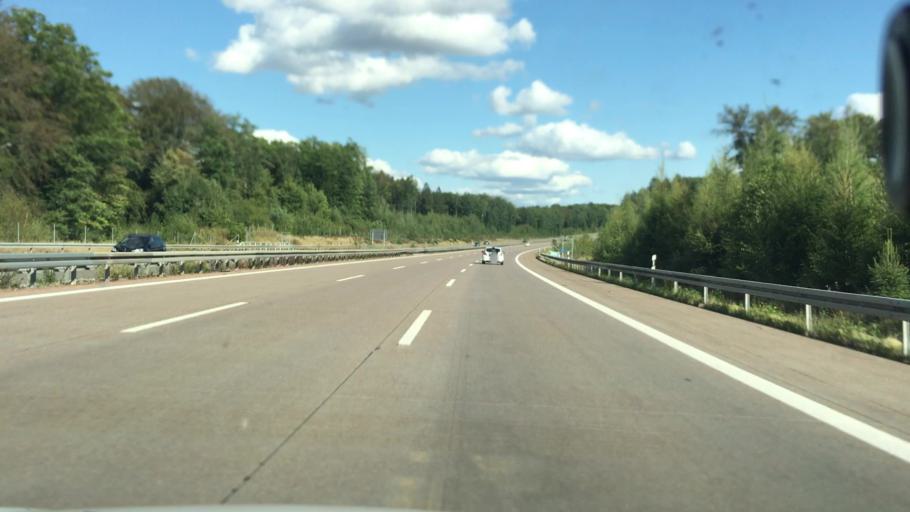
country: DE
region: Saxony
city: Hohenstein-Ernstthal
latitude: 50.8131
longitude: 12.6844
